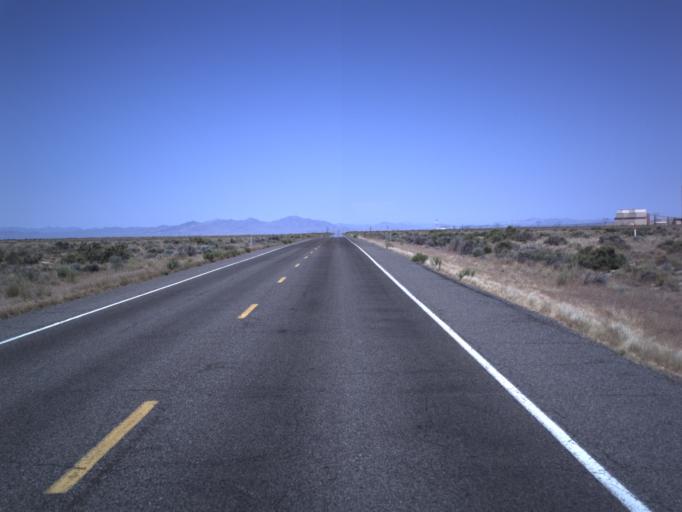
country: US
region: Utah
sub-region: Millard County
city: Delta
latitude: 39.4858
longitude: -112.5353
